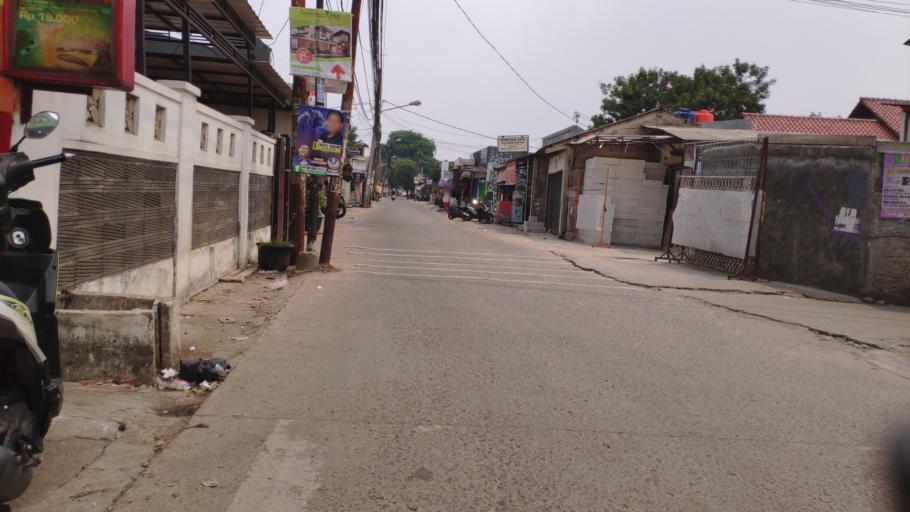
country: ID
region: West Java
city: Depok
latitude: -6.3723
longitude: 106.8007
